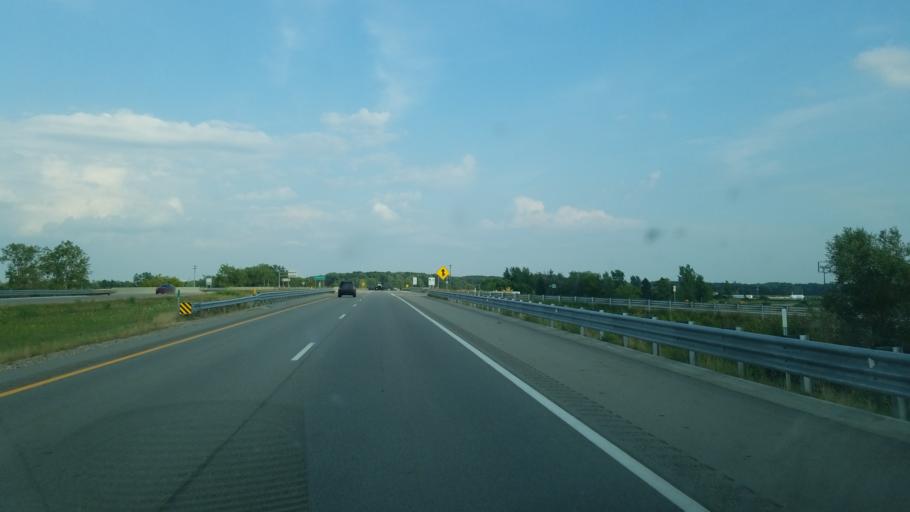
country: US
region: Michigan
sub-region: Gratiot County
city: Saint Louis
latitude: 43.3827
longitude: -84.6087
